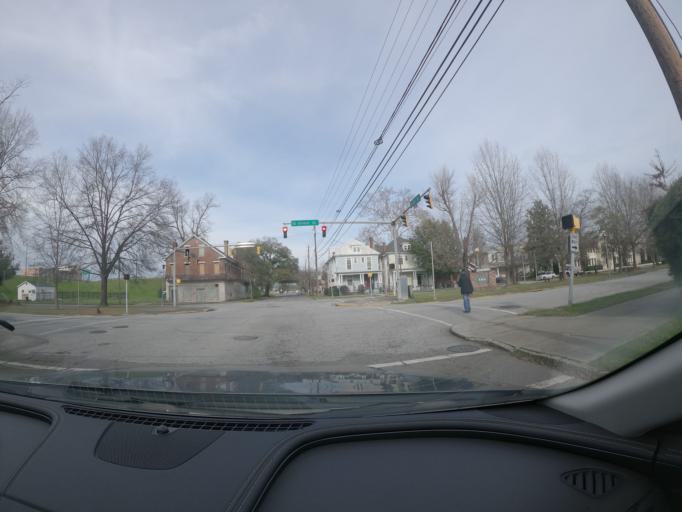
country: US
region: Georgia
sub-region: Richmond County
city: Augusta
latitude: 33.4699
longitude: -81.9573
